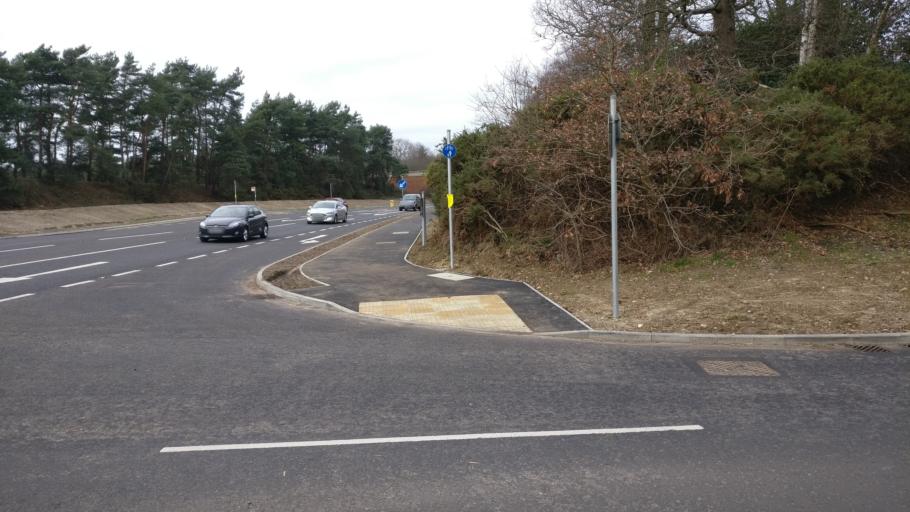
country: GB
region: England
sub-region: Hampshire
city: Fleet
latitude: 51.2925
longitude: -0.8689
